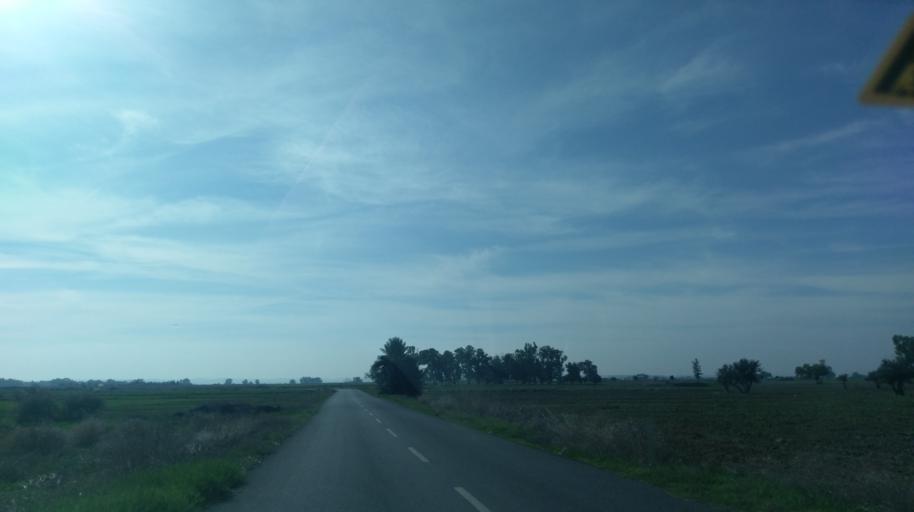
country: CY
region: Larnaka
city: Athienou
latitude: 35.1766
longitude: 33.5936
